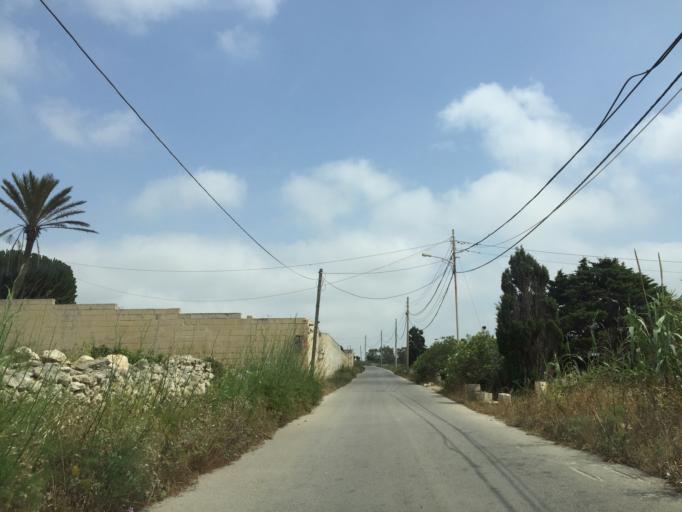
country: MT
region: L-Imgarr
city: Imgarr
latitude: 35.8998
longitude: 14.3527
